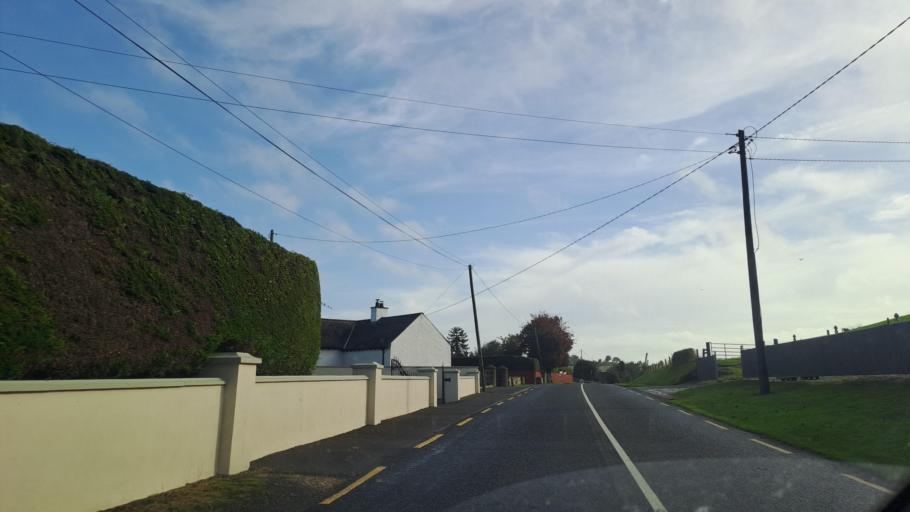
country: IE
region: Ulster
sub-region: County Monaghan
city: Carrickmacross
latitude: 53.9047
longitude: -6.6999
